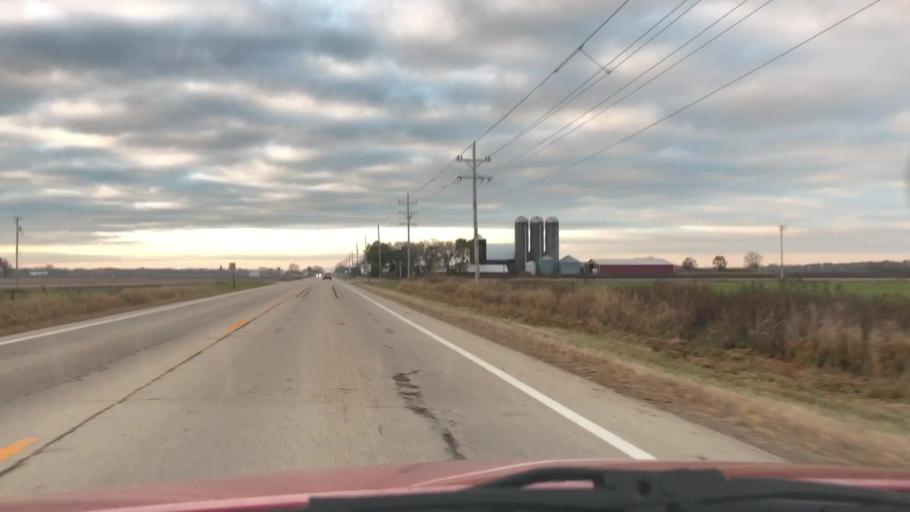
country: US
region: Wisconsin
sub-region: Outagamie County
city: Seymour
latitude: 44.4452
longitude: -88.2914
